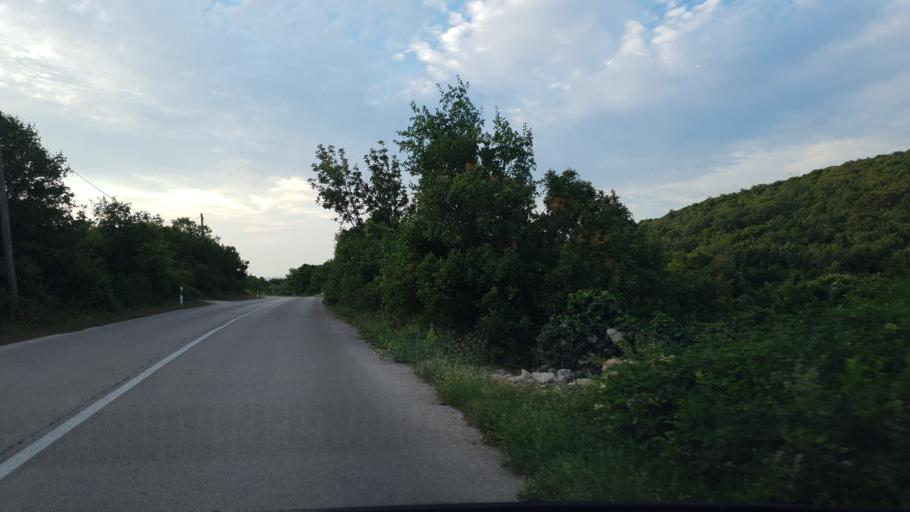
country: HR
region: Primorsko-Goranska
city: Punat
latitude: 44.9986
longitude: 14.6355
